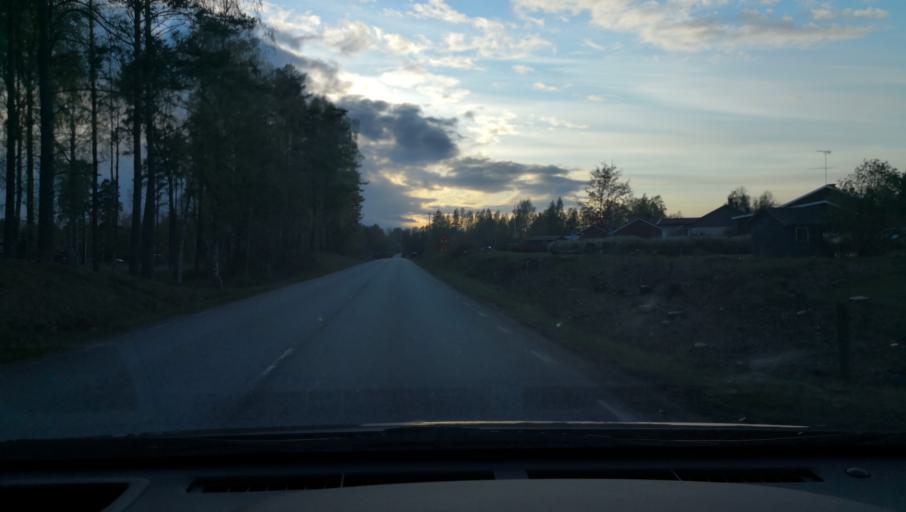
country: SE
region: OErebro
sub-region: Askersunds Kommun
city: Asbro
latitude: 58.9231
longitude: 15.0454
